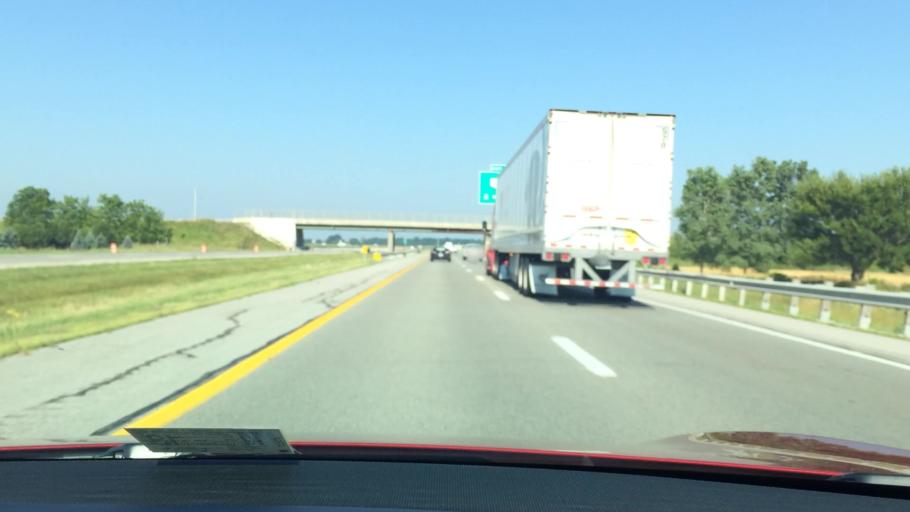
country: US
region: Ohio
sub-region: Fulton County
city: Wauseon
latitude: 41.5909
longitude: -84.0987
